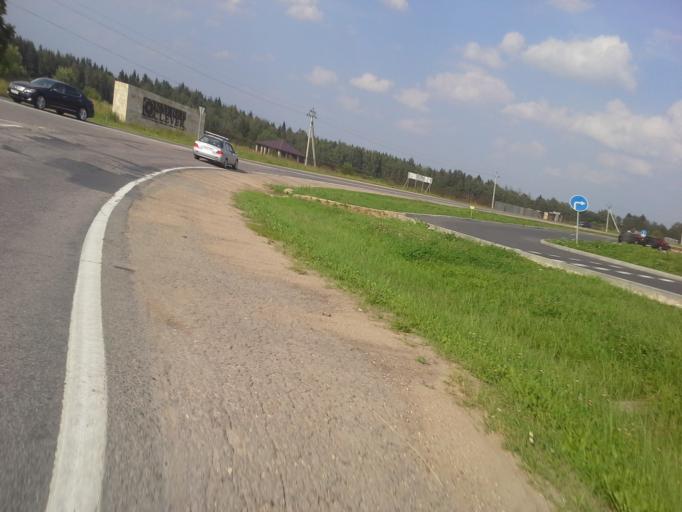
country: RU
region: Moskovskaya
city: Istra
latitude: 55.8809
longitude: 36.7987
